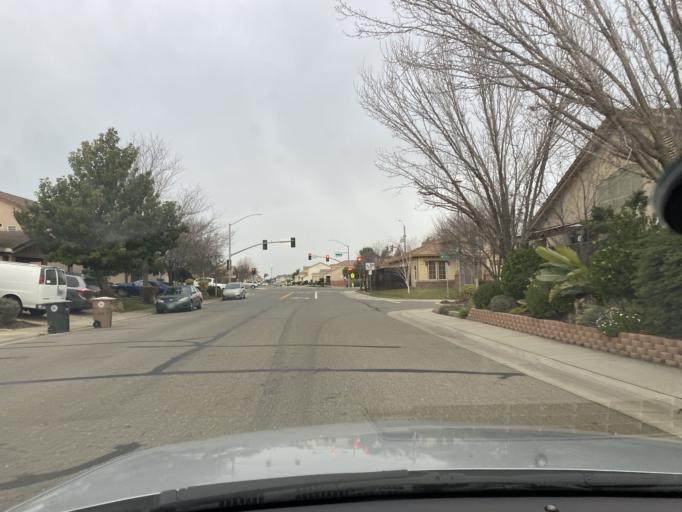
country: US
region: California
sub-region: Sacramento County
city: Elk Grove
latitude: 38.4405
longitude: -121.3910
